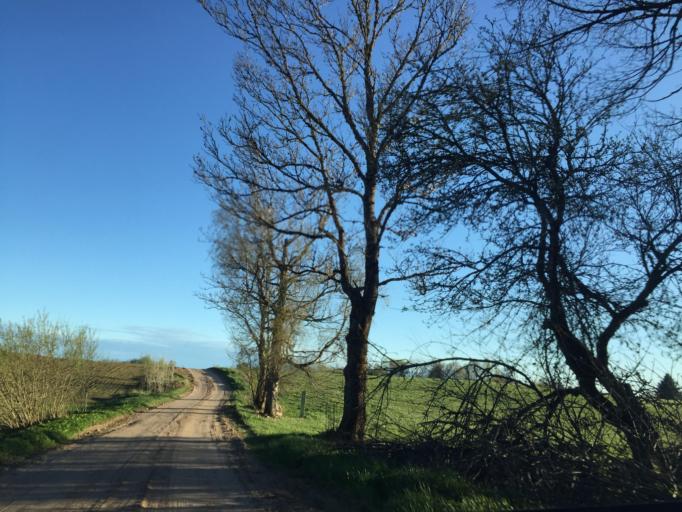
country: LV
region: Vecpiebalga
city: Vecpiebalga
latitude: 56.8445
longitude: 25.9570
